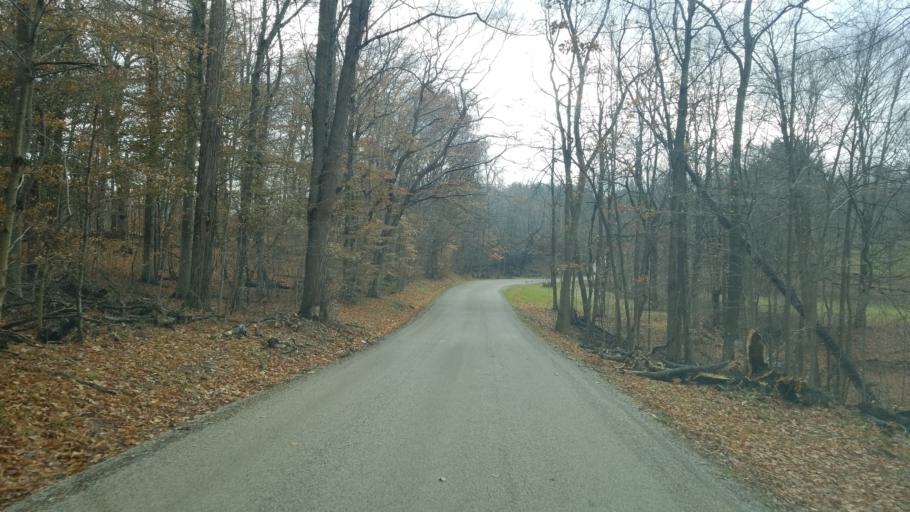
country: US
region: Ohio
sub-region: Richland County
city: Lincoln Heights
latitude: 40.8230
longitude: -82.4702
